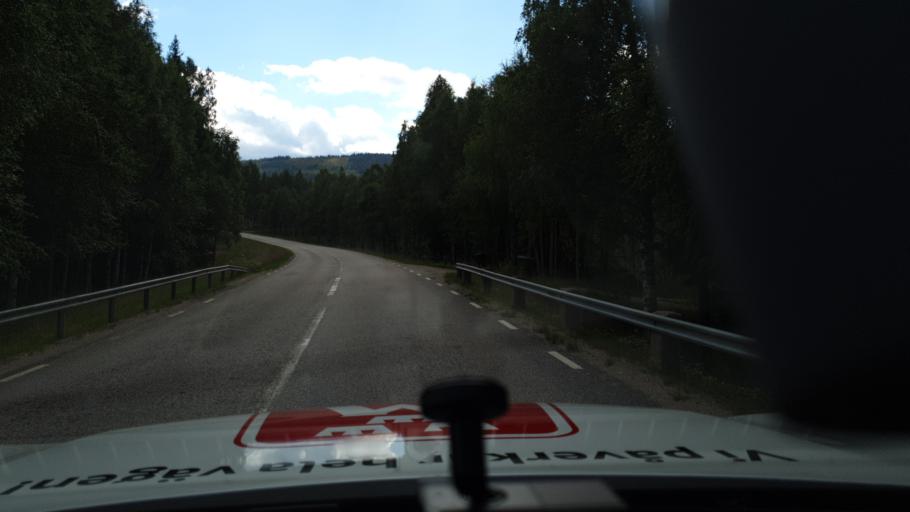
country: NO
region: Hedmark
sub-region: Trysil
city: Innbygda
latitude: 61.0293
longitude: 12.4705
